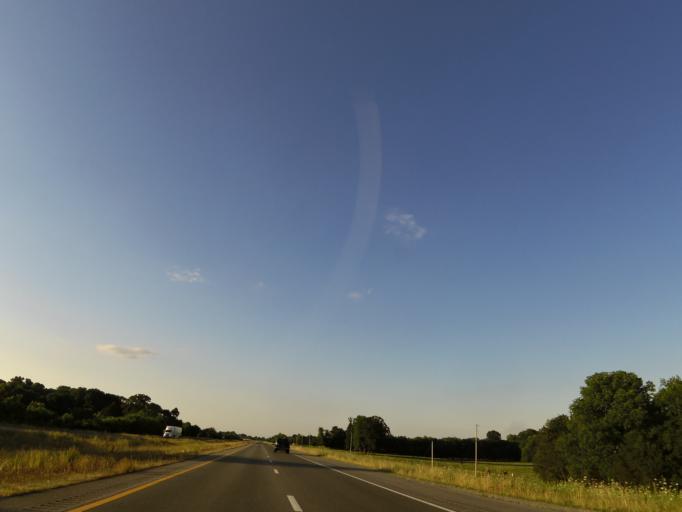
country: US
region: Tennessee
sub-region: Wilson County
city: Lebanon
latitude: 36.1593
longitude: -86.3591
